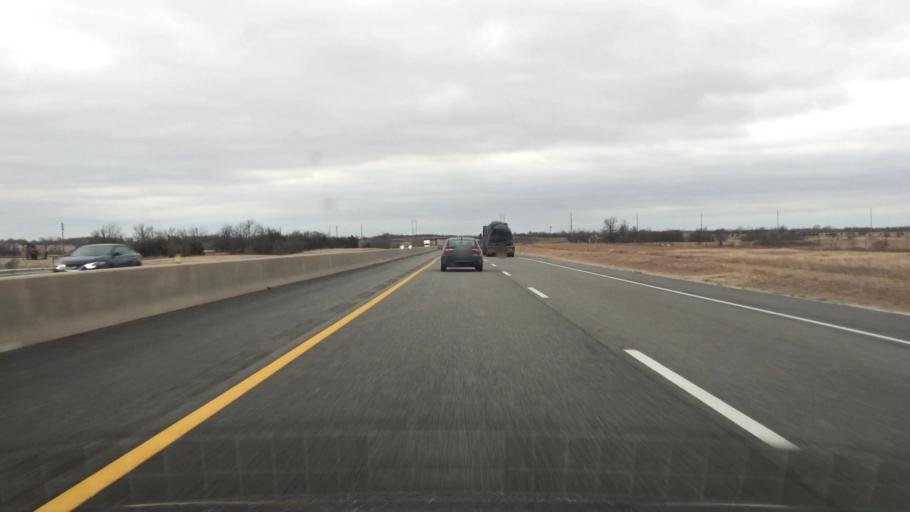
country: US
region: Kansas
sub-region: Butler County
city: El Dorado
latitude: 37.8005
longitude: -96.9266
